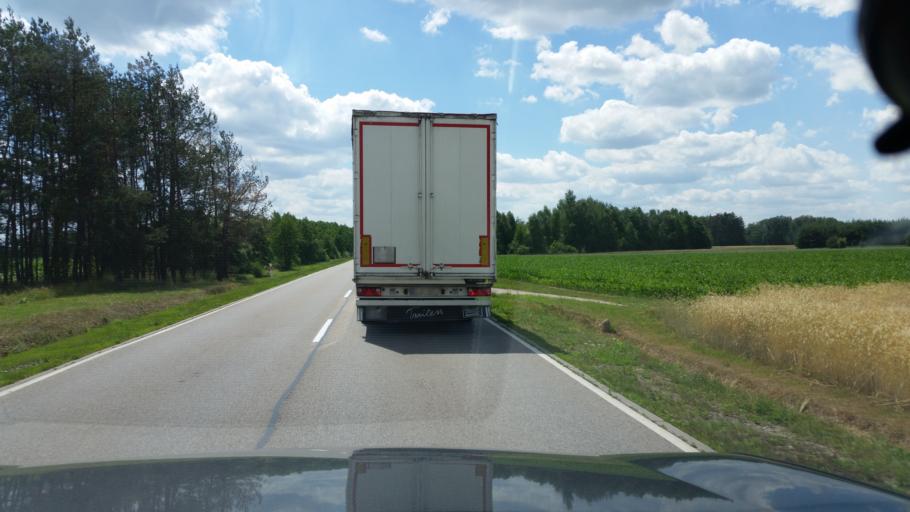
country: PL
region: Podlasie
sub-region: Powiat lomzynski
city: Sniadowo
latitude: 52.9651
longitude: 21.8947
